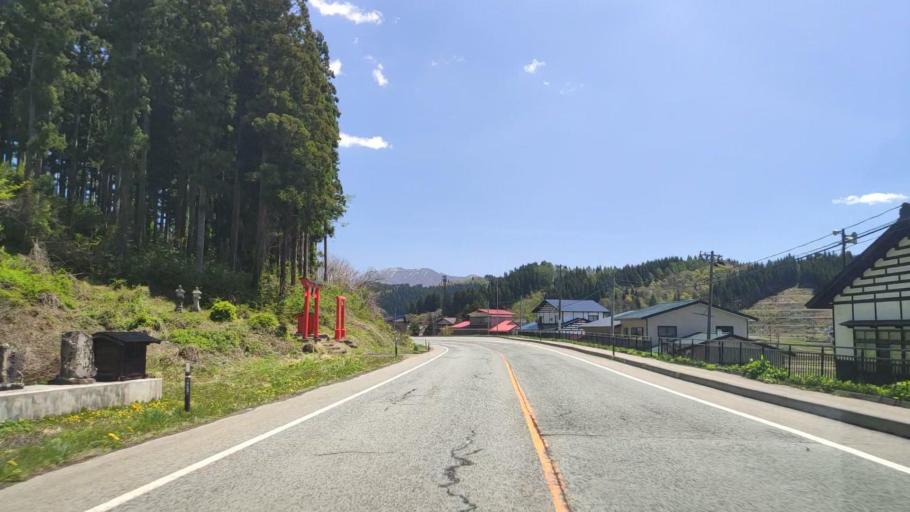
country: JP
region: Yamagata
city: Shinjo
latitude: 38.8896
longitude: 140.3256
